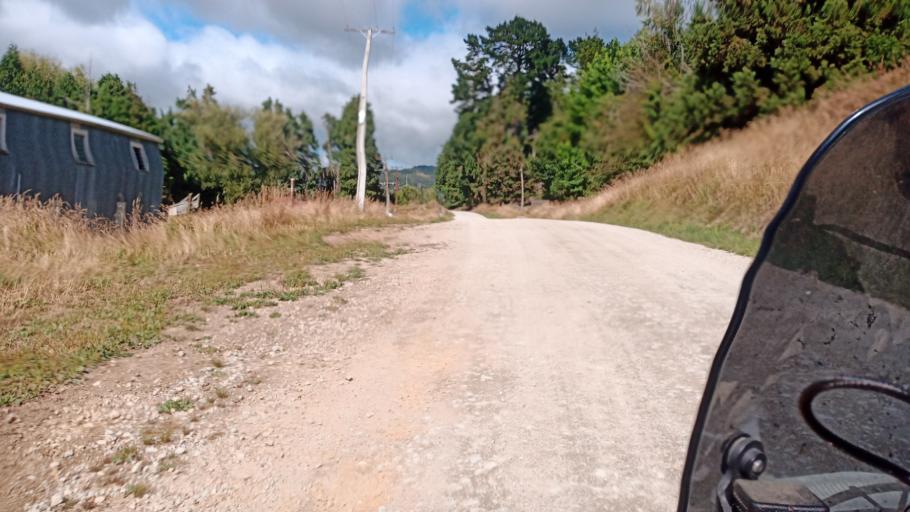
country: NZ
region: Hawke's Bay
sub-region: Wairoa District
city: Wairoa
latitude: -38.6076
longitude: 177.4494
